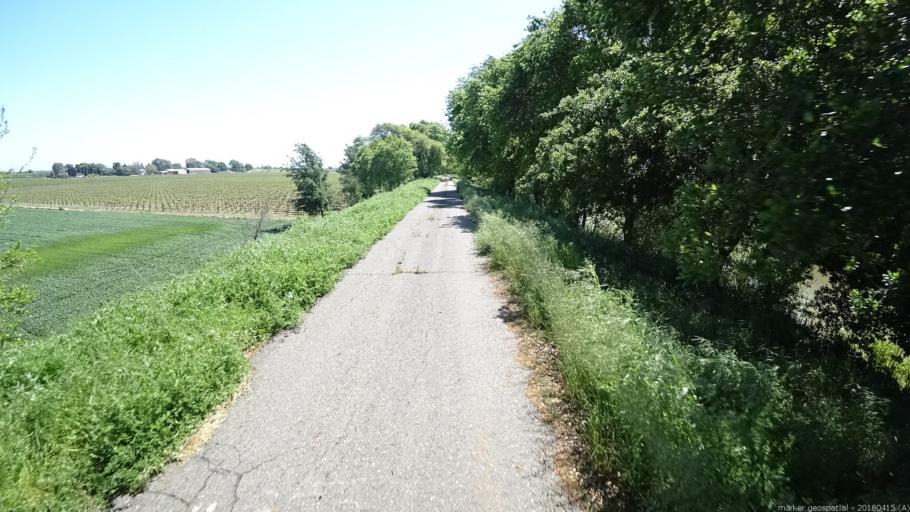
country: US
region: California
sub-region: Sacramento County
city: Walnut Grove
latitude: 38.2651
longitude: -121.6015
